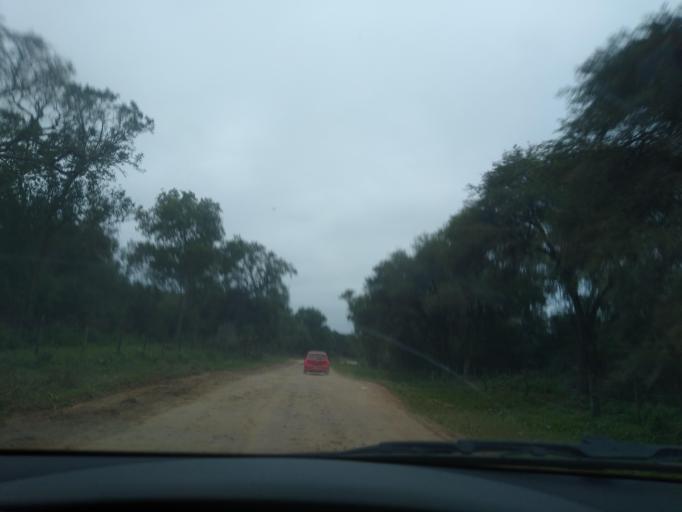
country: AR
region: Chaco
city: Colonia Benitez
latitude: -27.3457
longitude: -58.9703
